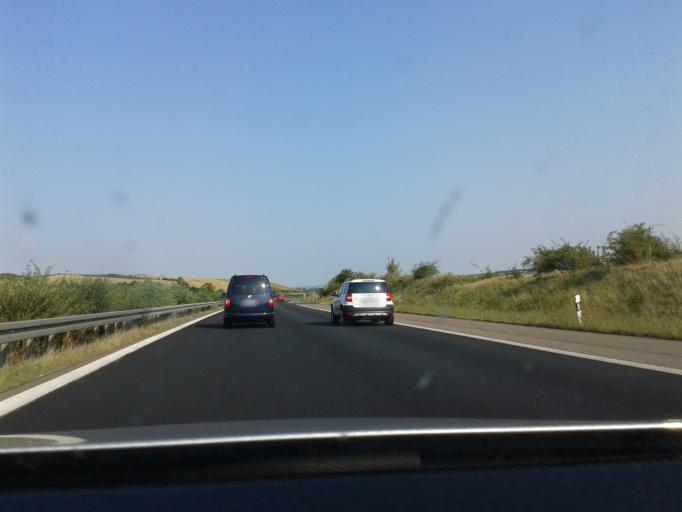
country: DE
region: Saxony-Anhalt
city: Bennungen
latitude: 51.4677
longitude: 11.1208
